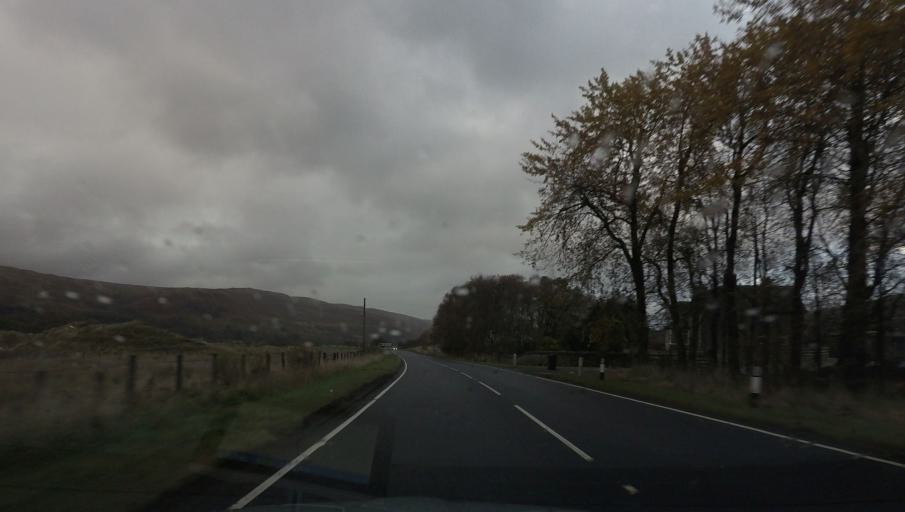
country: GB
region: Scotland
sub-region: Stirling
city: Callander
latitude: 56.4219
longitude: -4.4251
